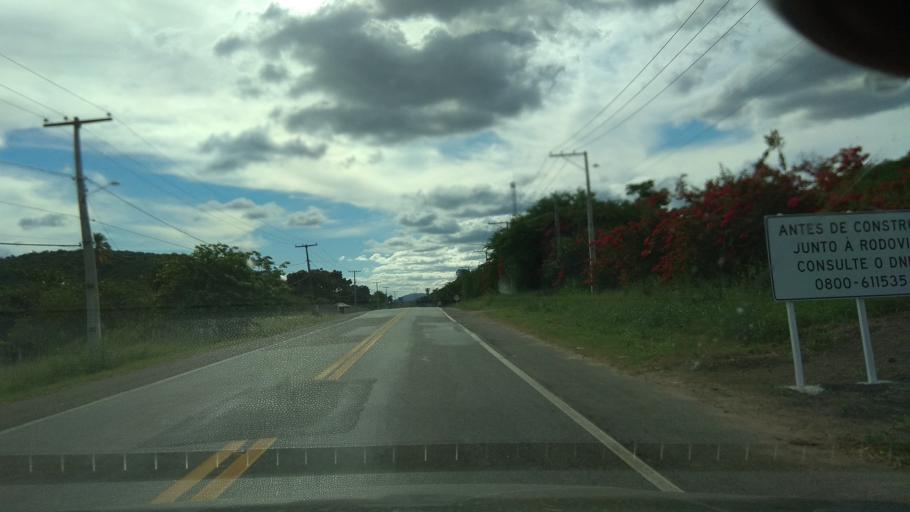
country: BR
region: Bahia
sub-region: Jequie
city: Jequie
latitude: -13.8778
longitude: -40.0370
